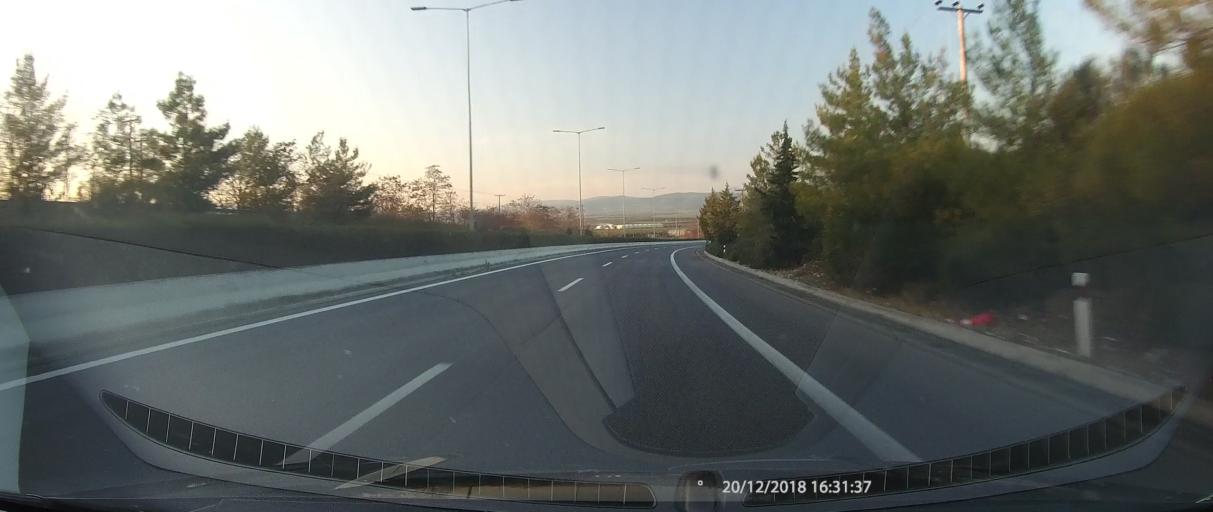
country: GR
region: Thessaly
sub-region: Nomos Magnisias
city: Evxinoupolis
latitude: 39.2291
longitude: 22.7393
